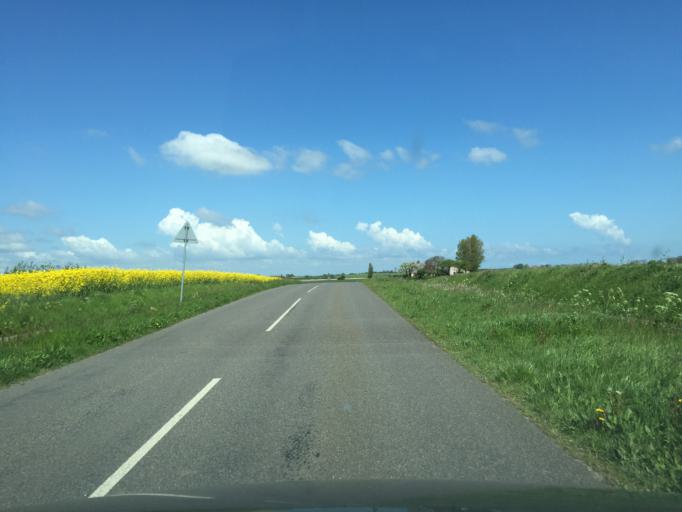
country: DK
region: Zealand
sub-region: Vordingborg Kommune
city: Stege
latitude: 55.0053
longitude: 12.2835
